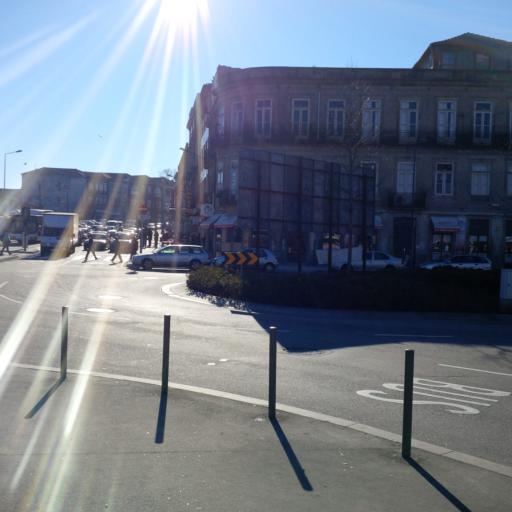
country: PT
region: Porto
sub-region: Vila Nova de Gaia
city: Oliveira do Douro
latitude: 41.1491
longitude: -8.5861
